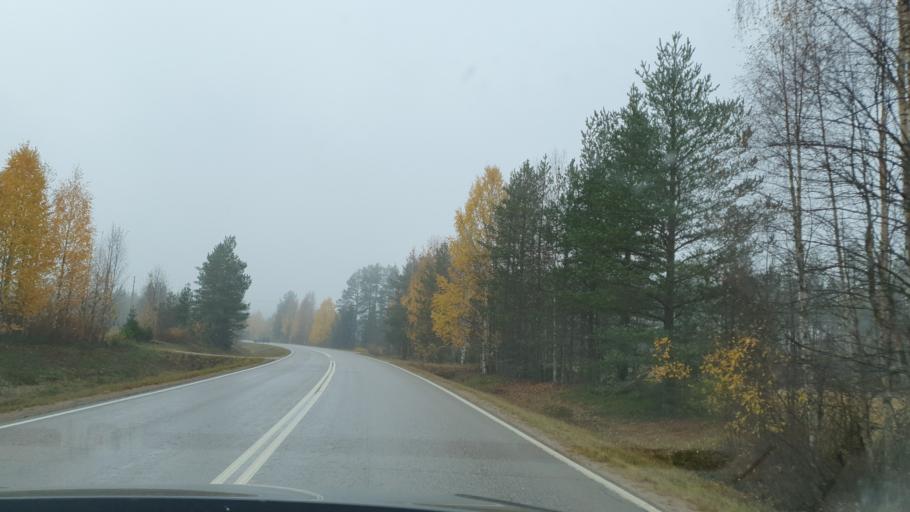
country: FI
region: Lapland
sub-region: Rovaniemi
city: Rovaniemi
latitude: 66.8198
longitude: 25.3953
